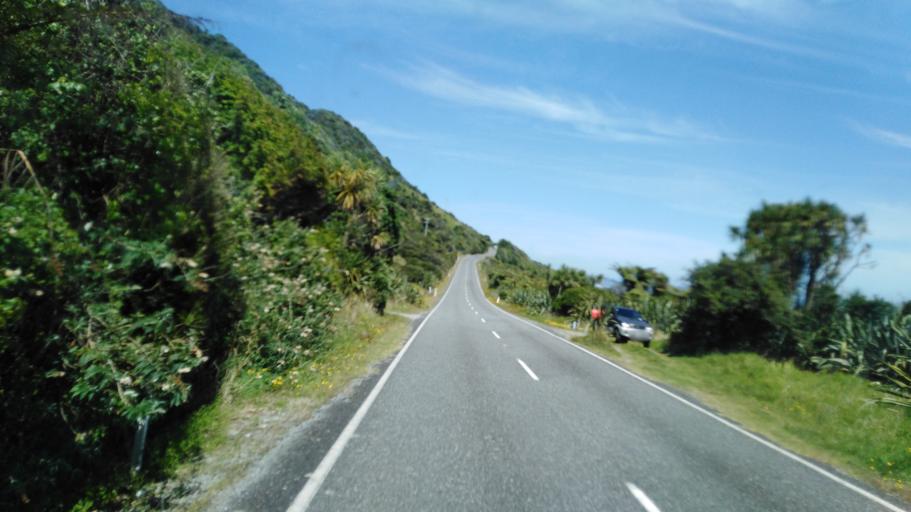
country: NZ
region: West Coast
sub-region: Buller District
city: Westport
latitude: -41.5685
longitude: 171.9085
